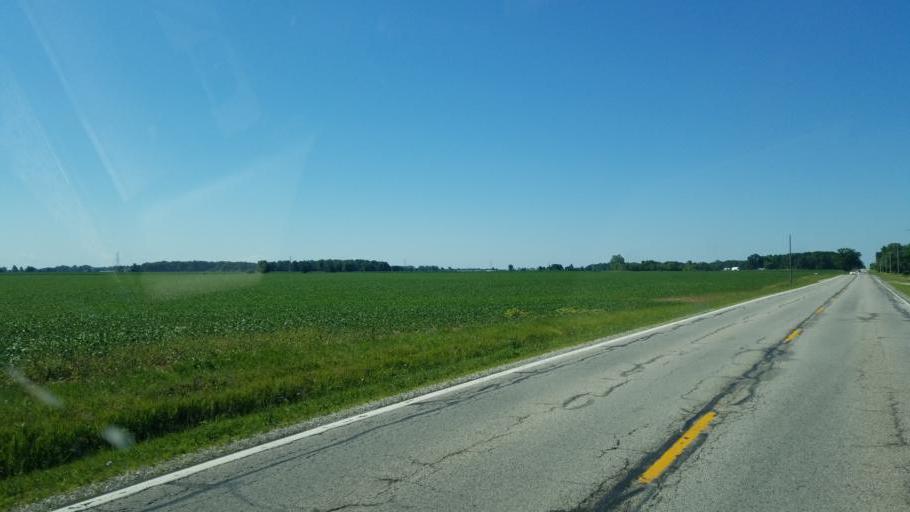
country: US
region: Ohio
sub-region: Marion County
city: Marion
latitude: 40.6799
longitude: -83.0997
